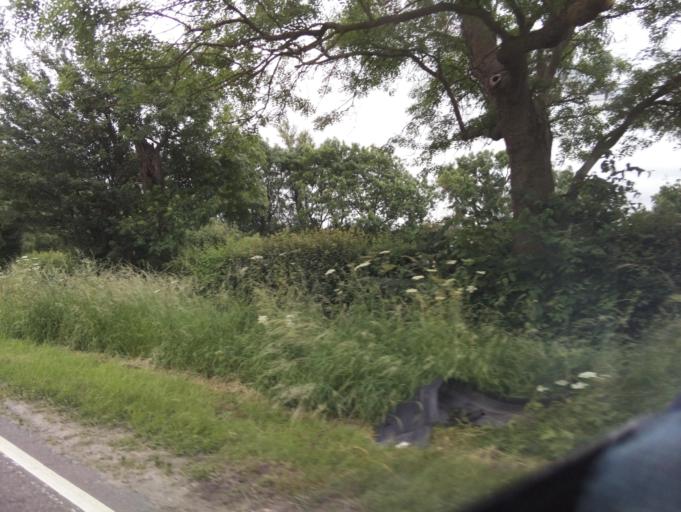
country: GB
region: England
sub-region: Nottinghamshire
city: East Leake
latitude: 52.8110
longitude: -1.1245
